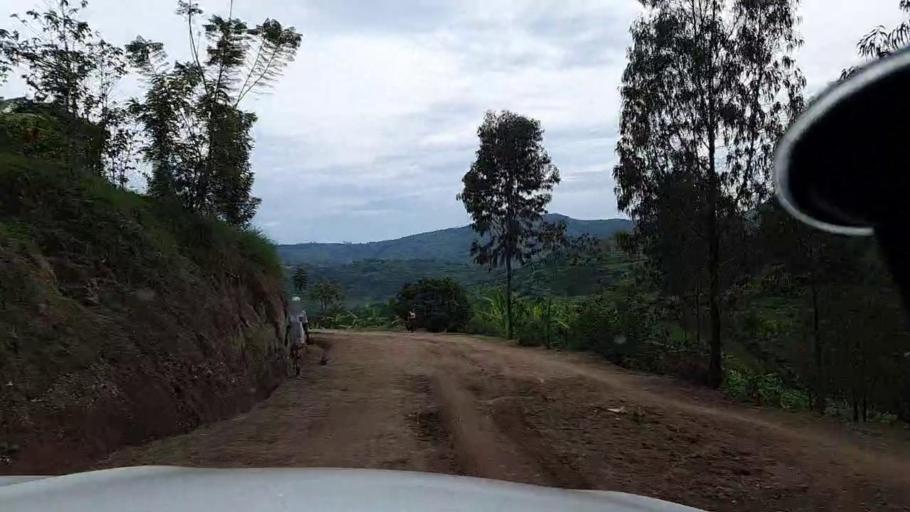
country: RW
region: Southern Province
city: Gitarama
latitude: -2.1326
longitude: 29.6610
